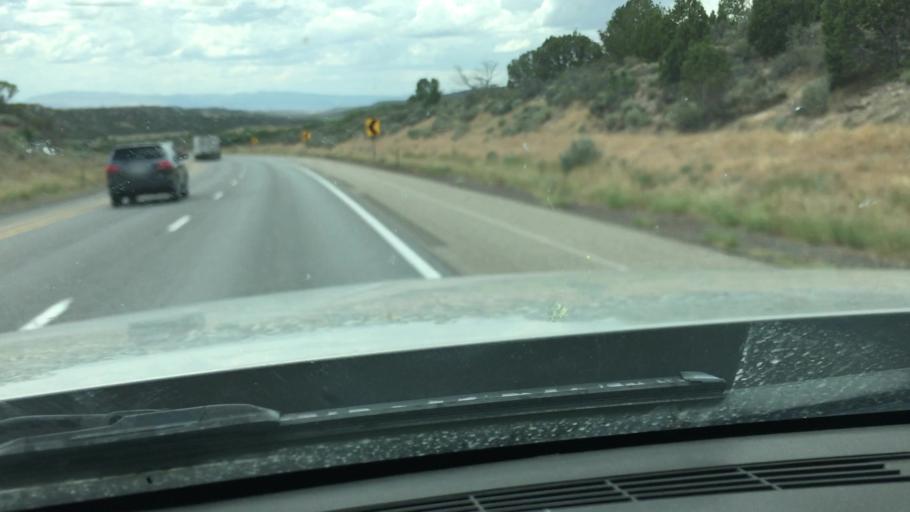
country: US
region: Utah
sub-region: Beaver County
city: Beaver
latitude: 38.4466
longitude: -112.6300
